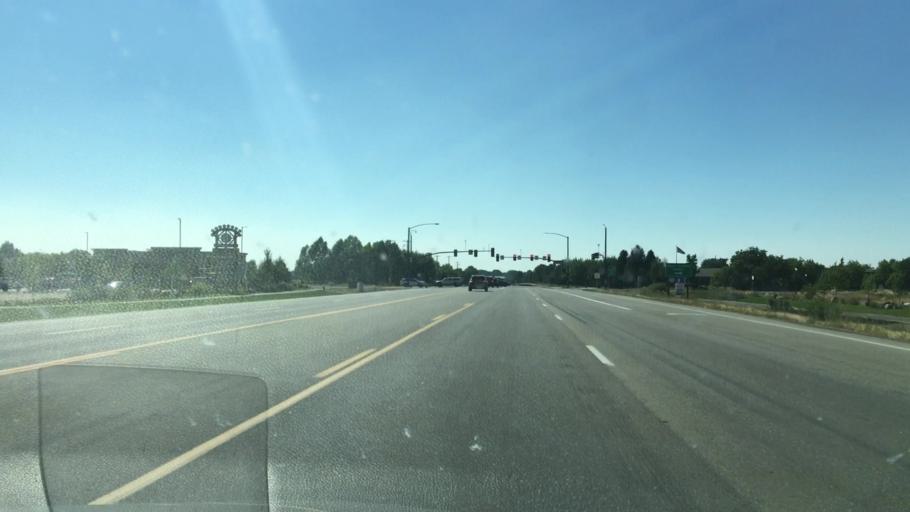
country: US
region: Idaho
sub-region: Ada County
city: Eagle
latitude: 43.6878
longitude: -116.3323
